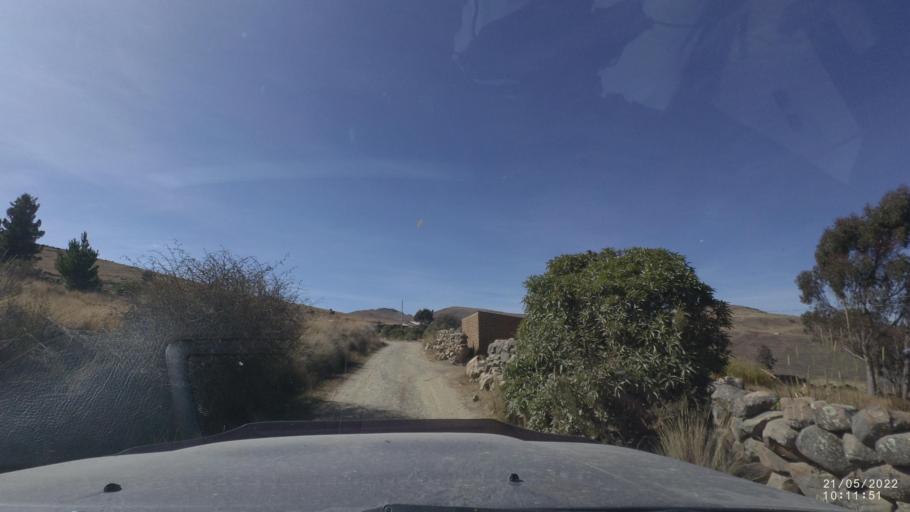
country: BO
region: Cochabamba
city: Colomi
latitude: -17.3315
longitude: -65.9798
